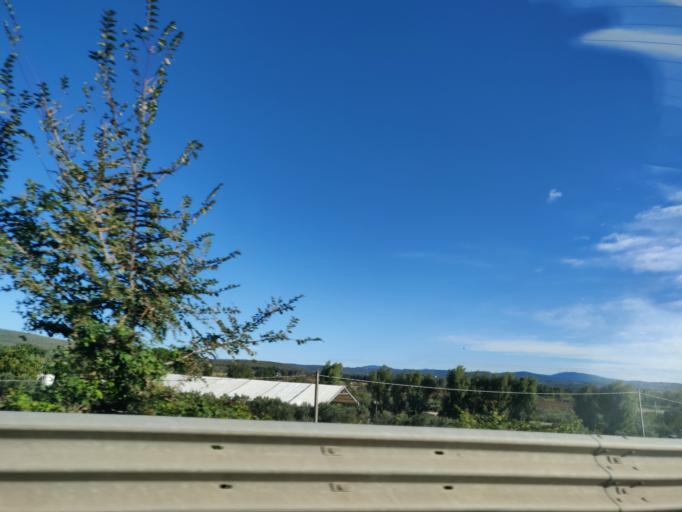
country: IT
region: Tuscany
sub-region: Provincia di Grosseto
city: Scarlino Scalo
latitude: 42.9586
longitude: 10.8008
